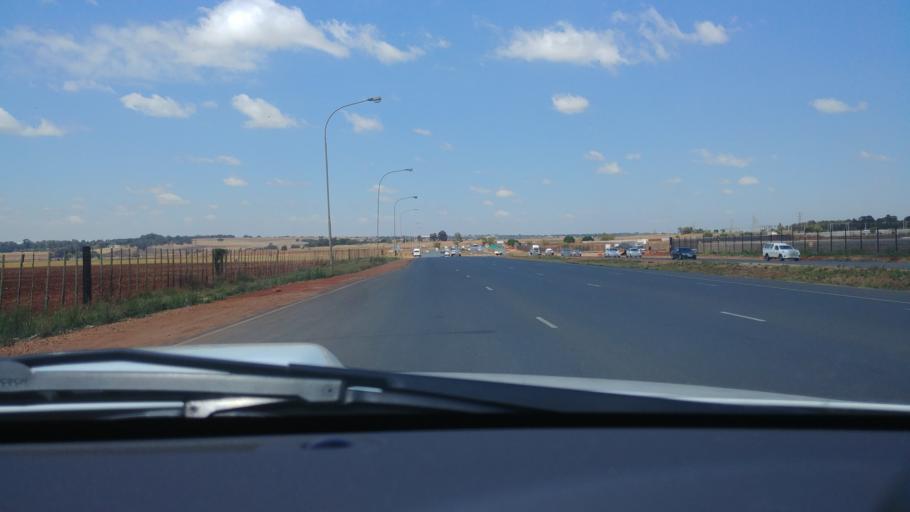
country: ZA
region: Gauteng
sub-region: Ekurhuleni Metropolitan Municipality
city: Tembisa
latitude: -26.0343
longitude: 28.2584
